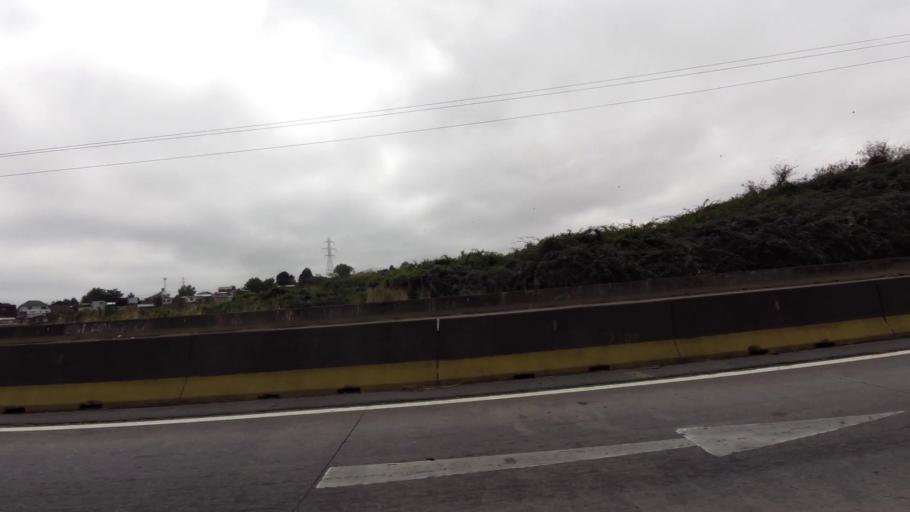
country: CL
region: Biobio
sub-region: Provincia de Concepcion
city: Concepcion
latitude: -36.7989
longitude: -73.0463
